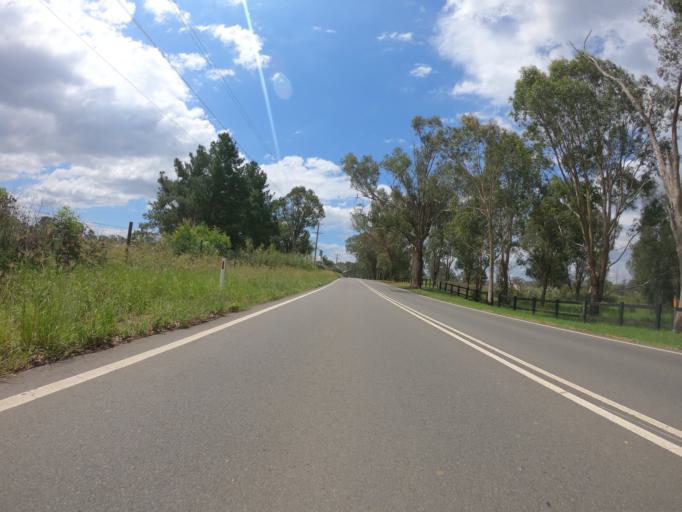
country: AU
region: New South Wales
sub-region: Penrith Municipality
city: Kingswood Park
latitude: -33.8315
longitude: 150.7578
